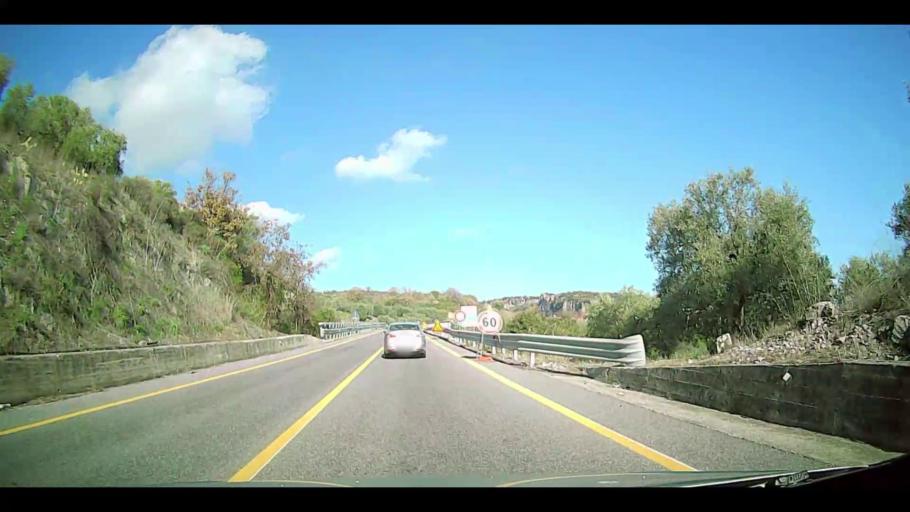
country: IT
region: Calabria
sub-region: Provincia di Crotone
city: Caccuri
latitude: 39.2206
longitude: 16.7942
